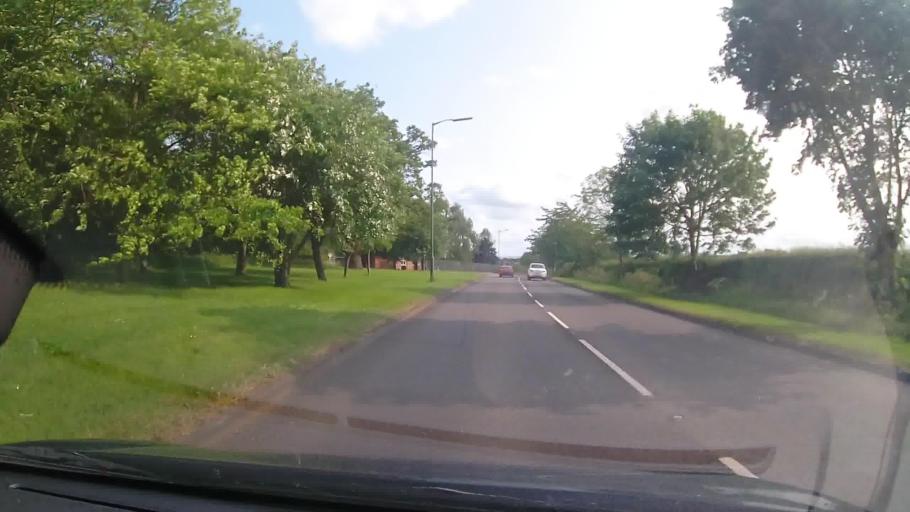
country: GB
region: England
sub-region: Shropshire
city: Shrewsbury
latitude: 52.7385
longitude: -2.7456
